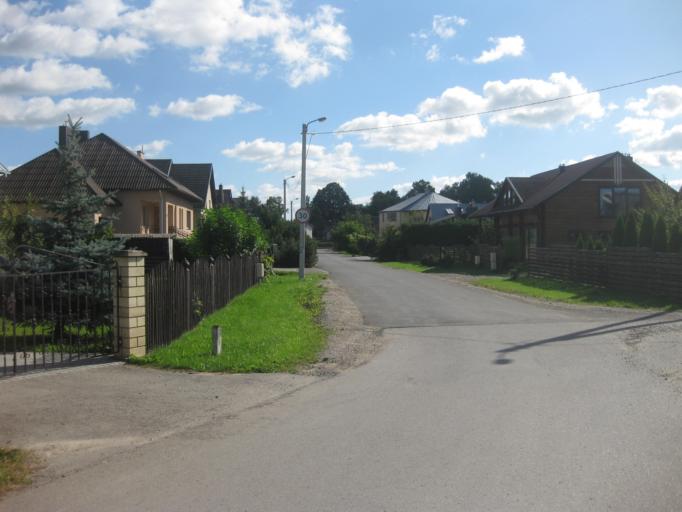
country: LT
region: Kauno apskritis
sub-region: Kauno rajonas
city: Garliava
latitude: 54.8332
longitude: 23.8669
